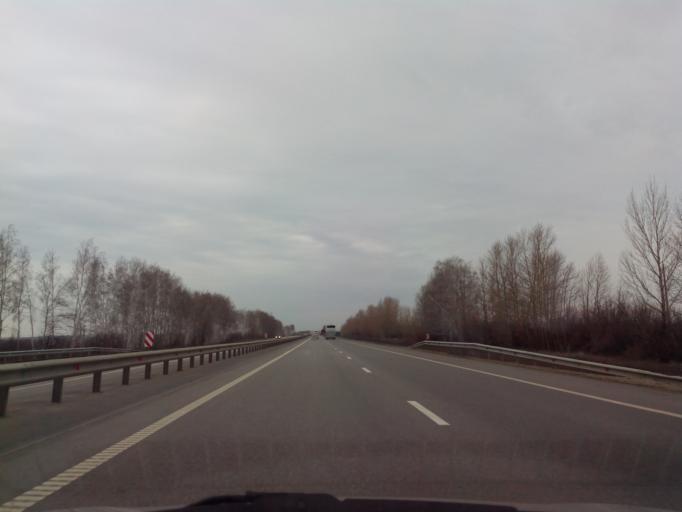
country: RU
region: Tambov
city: Selezni
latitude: 52.8092
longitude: 40.9593
